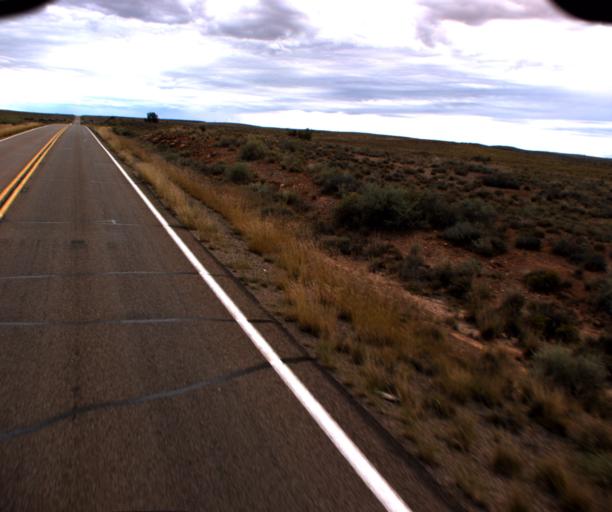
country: US
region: Arizona
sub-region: Navajo County
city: Holbrook
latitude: 34.8437
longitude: -110.1469
